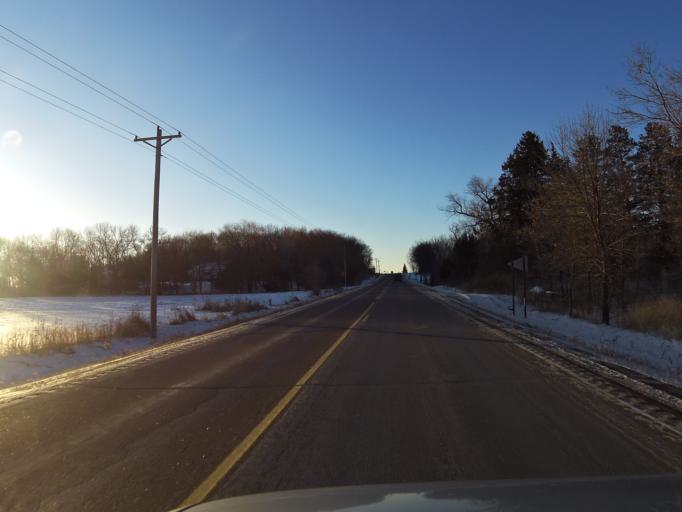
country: US
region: Minnesota
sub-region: Scott County
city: Prior Lake
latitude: 44.6845
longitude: -93.3793
